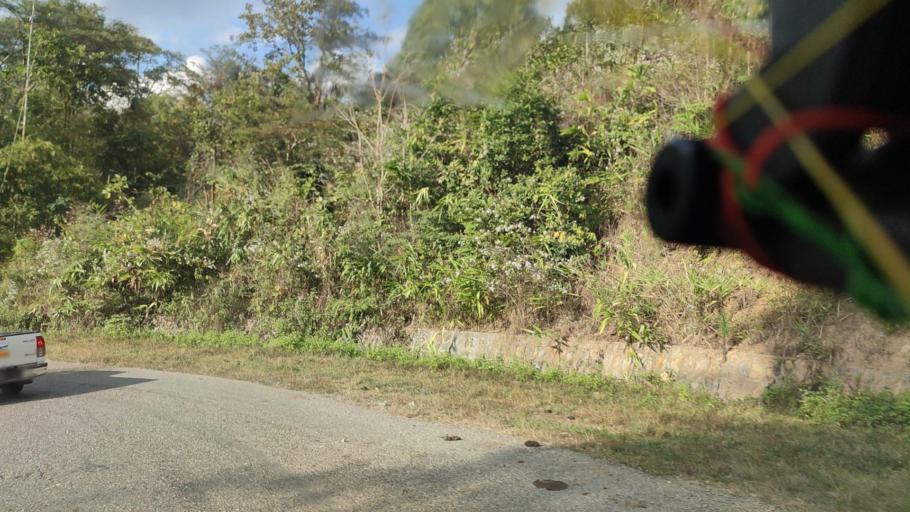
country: MM
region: Shan
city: Taunggyi
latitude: 21.4689
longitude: 97.5968
